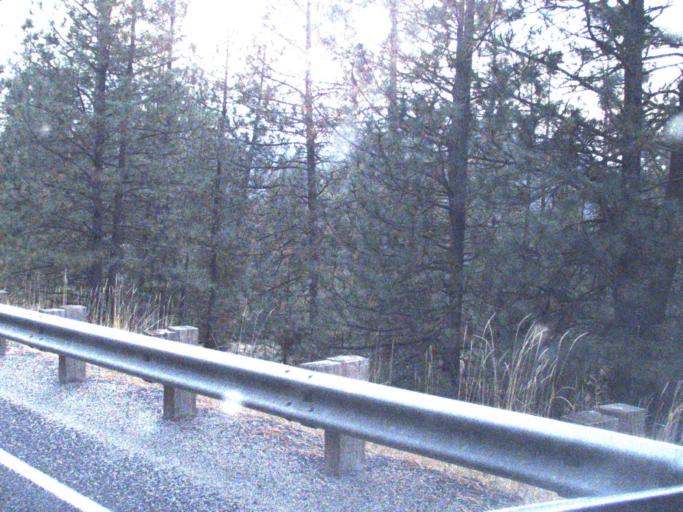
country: US
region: Washington
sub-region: Lincoln County
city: Davenport
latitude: 48.0363
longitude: -118.2297
